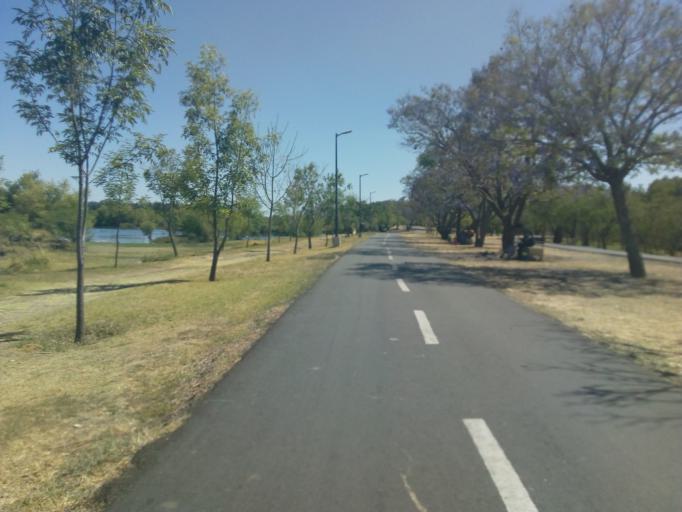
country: MX
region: Guanajuato
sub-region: Leon
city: La Ermita
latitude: 21.1825
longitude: -101.6958
